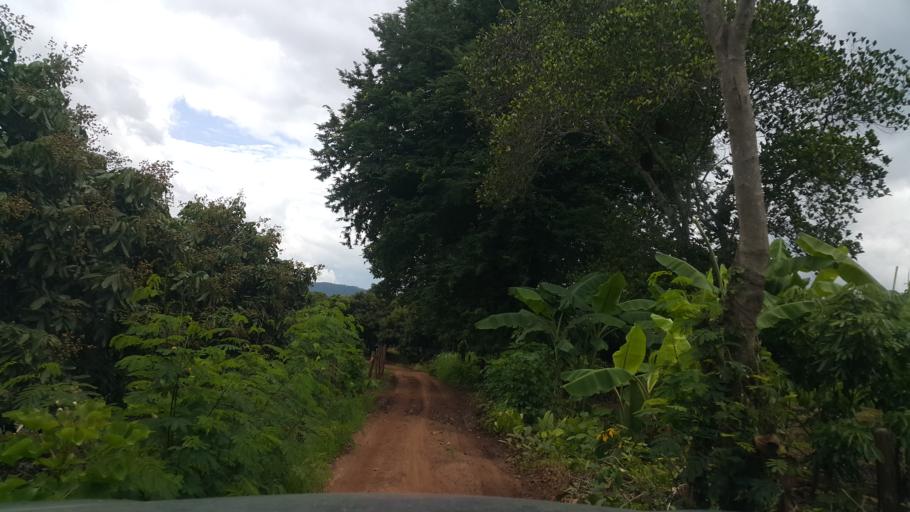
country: TH
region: Chiang Mai
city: Mae Taeng
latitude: 19.2304
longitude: 99.0001
